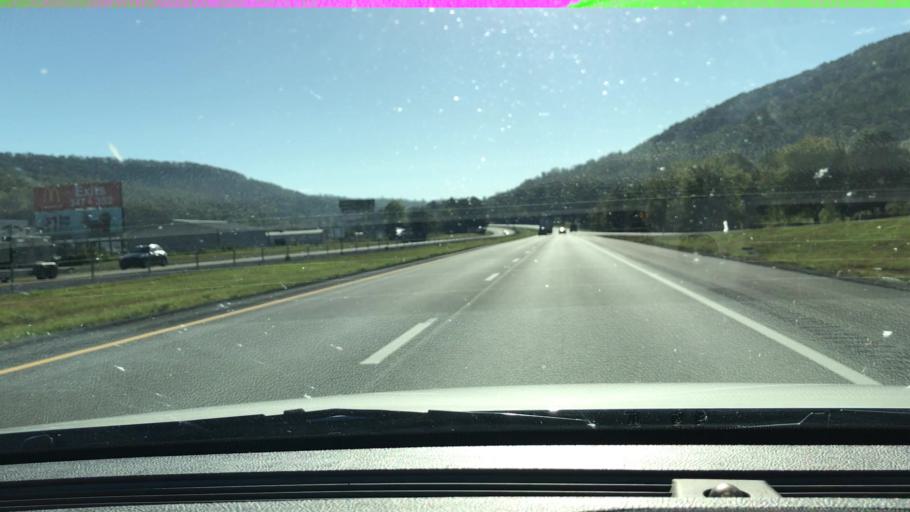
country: US
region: Tennessee
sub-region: Cumberland County
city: Fairfield Glade
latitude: 35.9045
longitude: -84.8752
